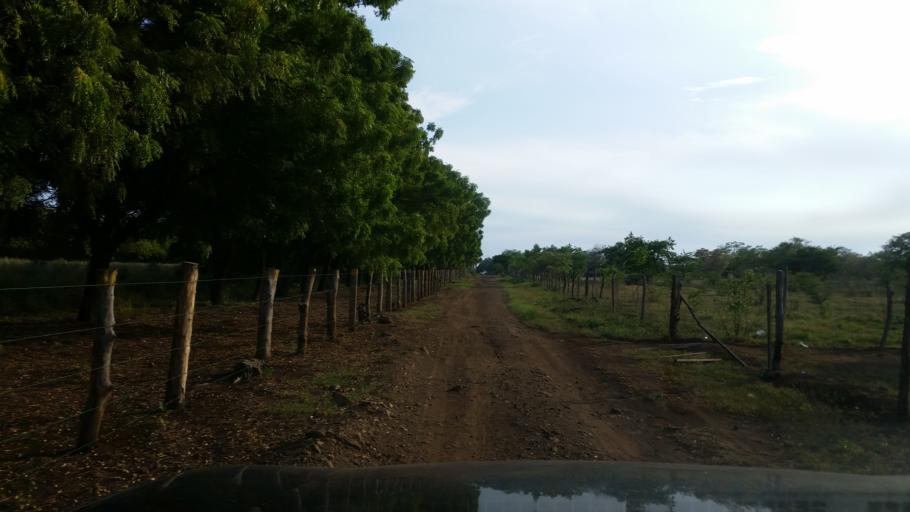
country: NI
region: Managua
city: Masachapa
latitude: 11.7670
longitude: -86.4922
